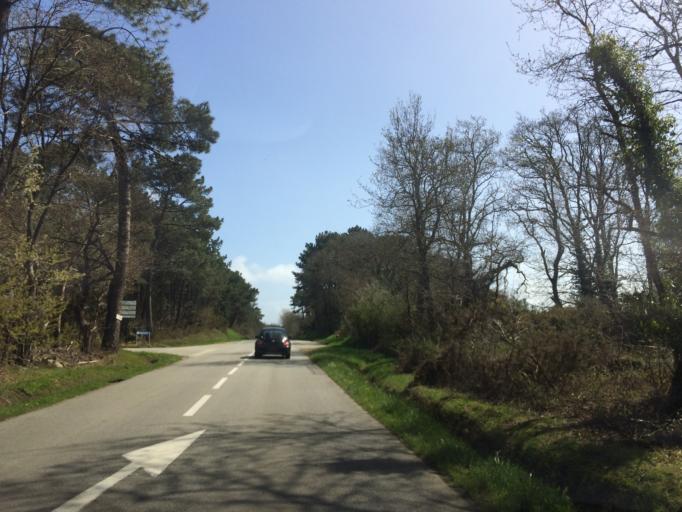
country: FR
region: Brittany
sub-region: Departement du Morbihan
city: La Trinite-sur-Mer
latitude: 47.6089
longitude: -3.0470
